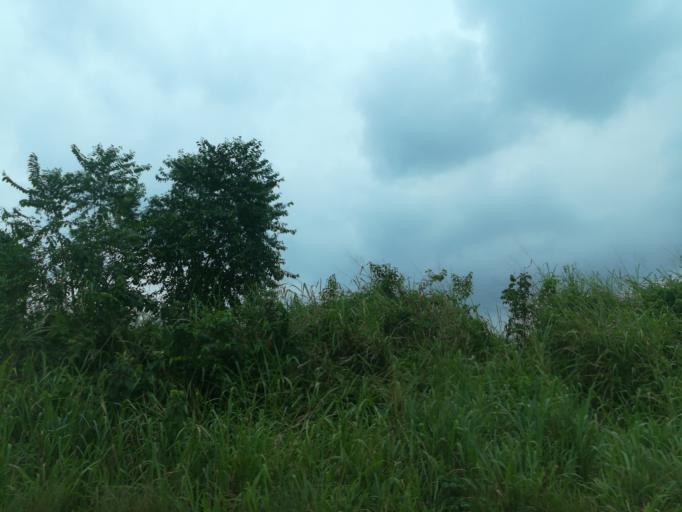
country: NG
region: Lagos
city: Ejirin
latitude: 6.6474
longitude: 3.7332
